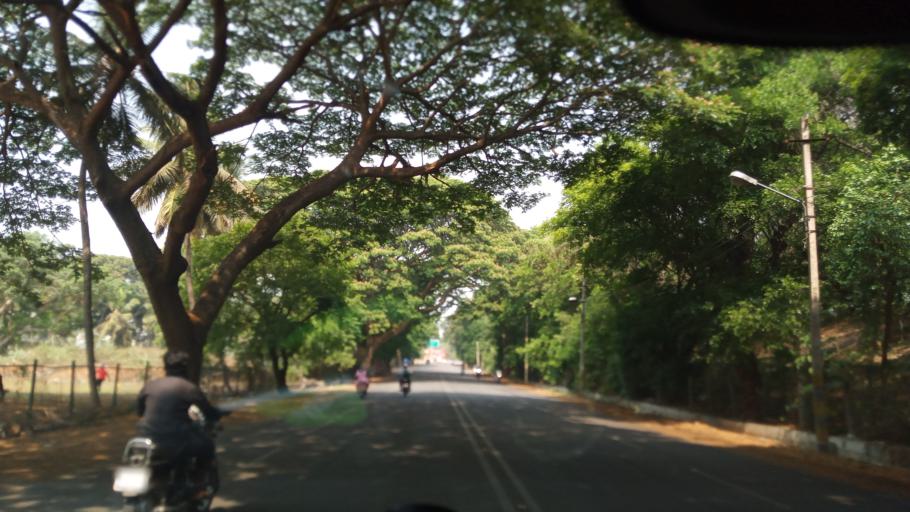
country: IN
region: Karnataka
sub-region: Mysore
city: Mysore
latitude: 12.3065
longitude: 76.6304
